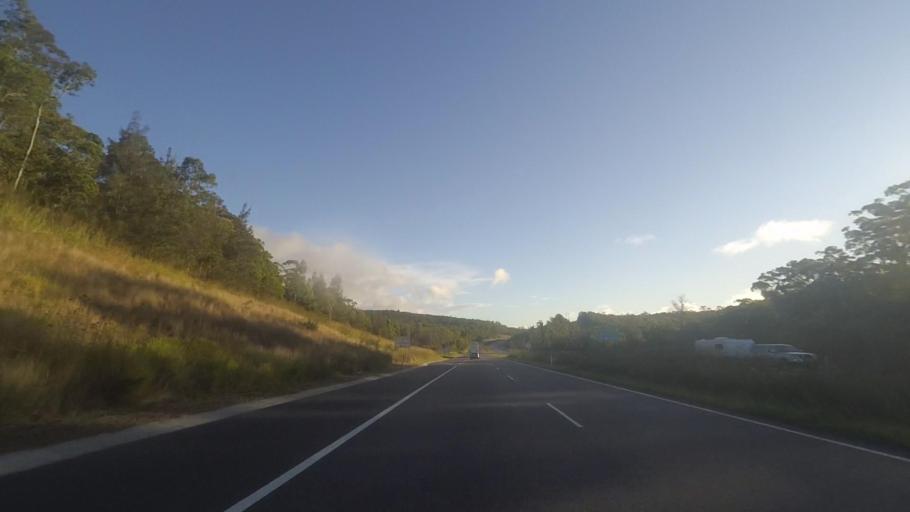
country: AU
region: New South Wales
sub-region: Great Lakes
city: Bulahdelah
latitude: -32.5090
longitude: 152.2110
